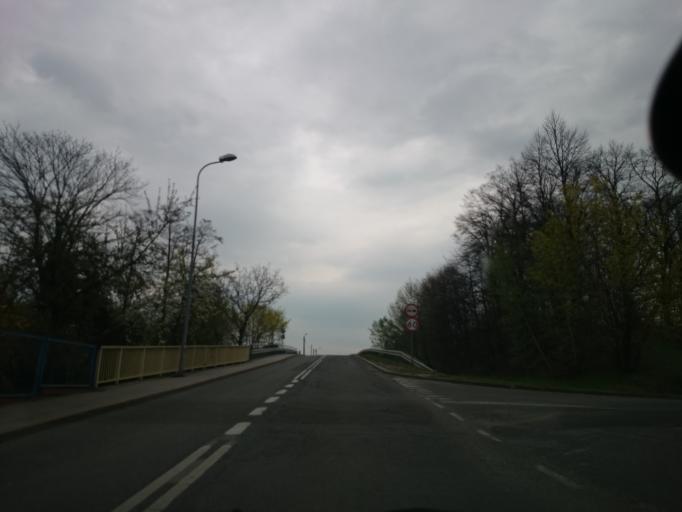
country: PL
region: Opole Voivodeship
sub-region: Powiat nyski
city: Glucholazy
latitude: 50.3172
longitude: 17.3956
